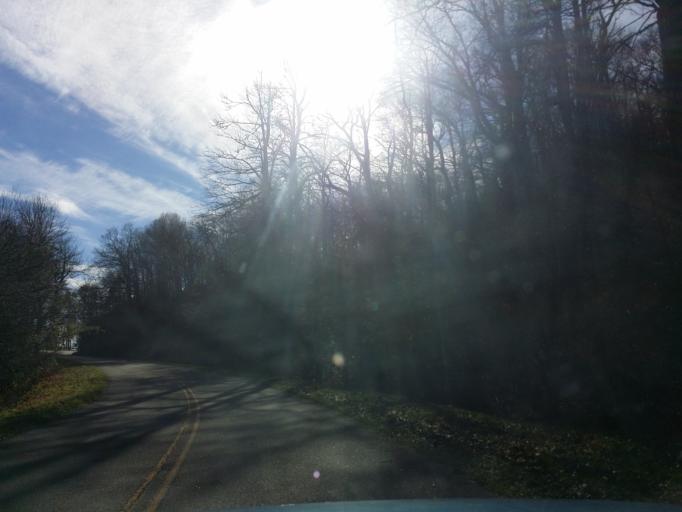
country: US
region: North Carolina
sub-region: Buncombe County
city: Black Mountain
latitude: 35.7316
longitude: -82.2039
